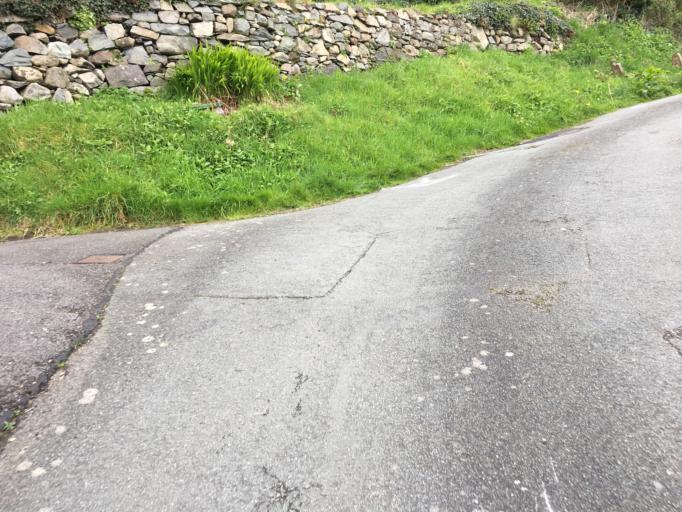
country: GB
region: Wales
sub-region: Gwynedd
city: Llanfair
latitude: 52.8607
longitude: -4.1071
